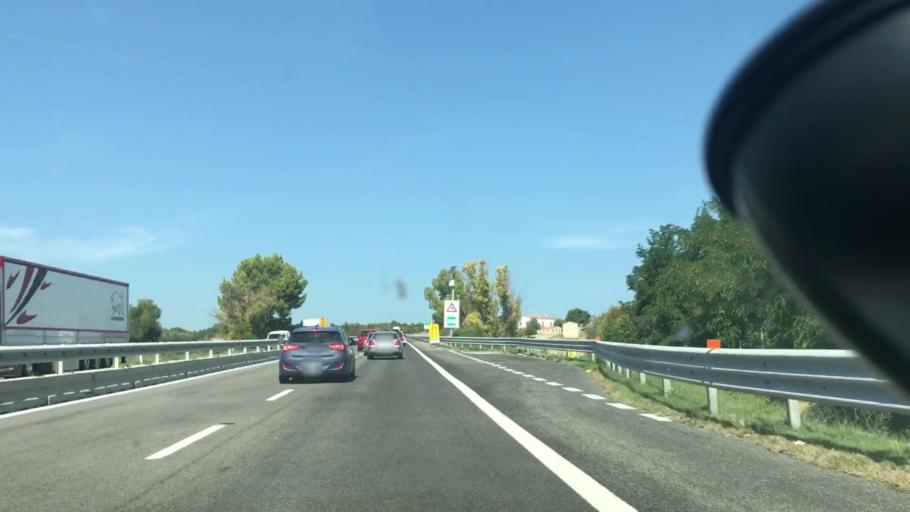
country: IT
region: Abruzzo
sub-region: Provincia di Chieti
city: San Salvo
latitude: 42.0679
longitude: 14.7263
